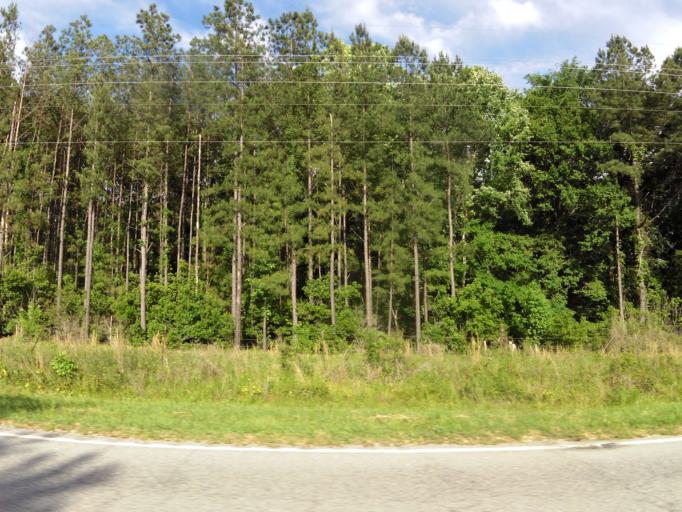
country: US
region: South Carolina
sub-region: Allendale County
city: Fairfax
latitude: 32.9045
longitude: -81.2378
